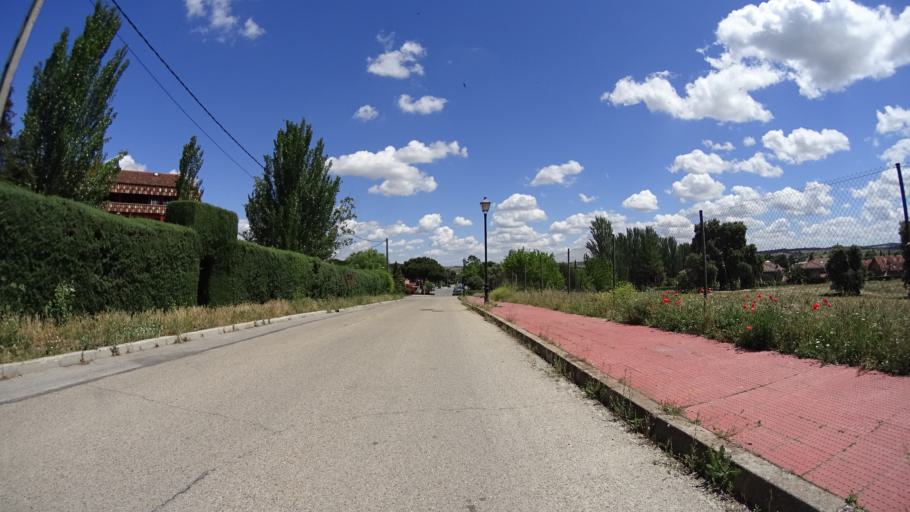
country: ES
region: Madrid
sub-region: Provincia de Madrid
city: Villanueva del Pardillo
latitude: 40.4644
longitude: -3.9504
